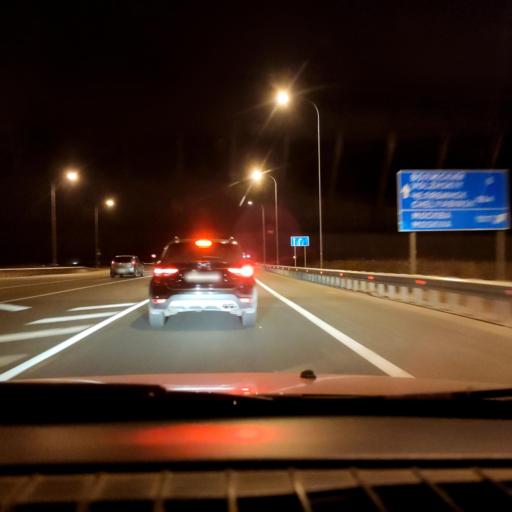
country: RU
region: Samara
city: Bereza
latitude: 53.4941
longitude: 50.1177
